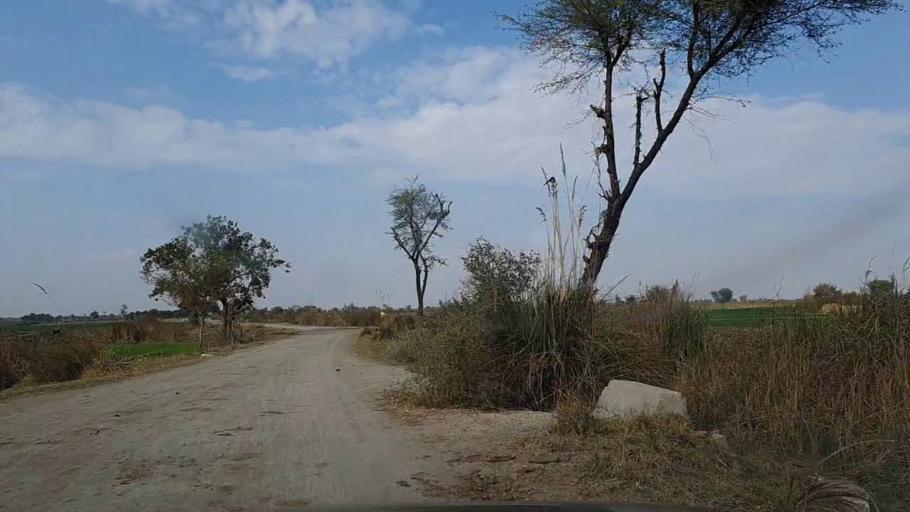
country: PK
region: Sindh
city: Sanghar
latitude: 26.2516
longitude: 69.0124
